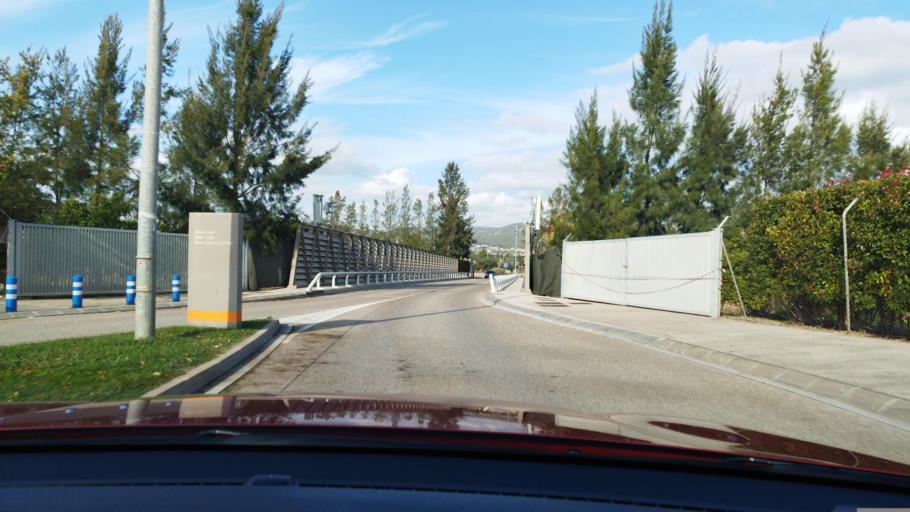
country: ES
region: Catalonia
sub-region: Provincia de Tarragona
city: Santa Oliva
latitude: 41.2676
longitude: 1.5236
